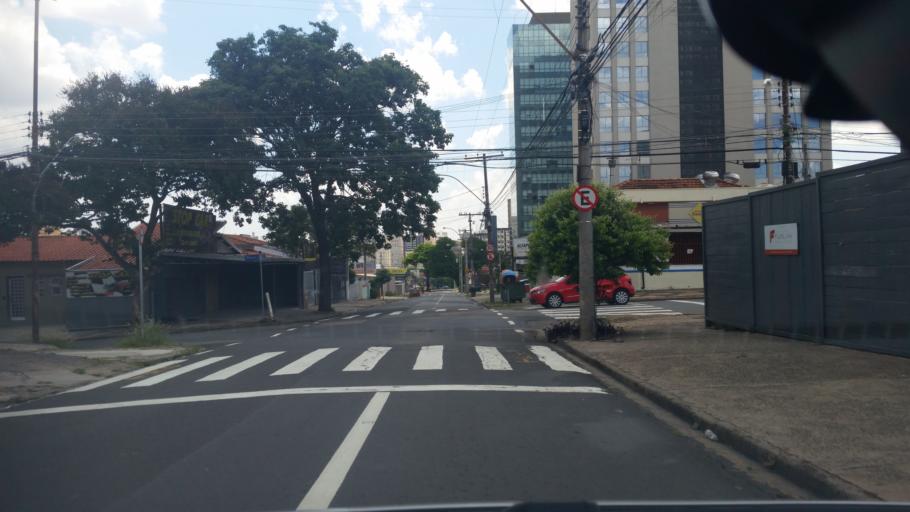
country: BR
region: Sao Paulo
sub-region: Campinas
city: Campinas
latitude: -22.8855
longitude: -47.0575
